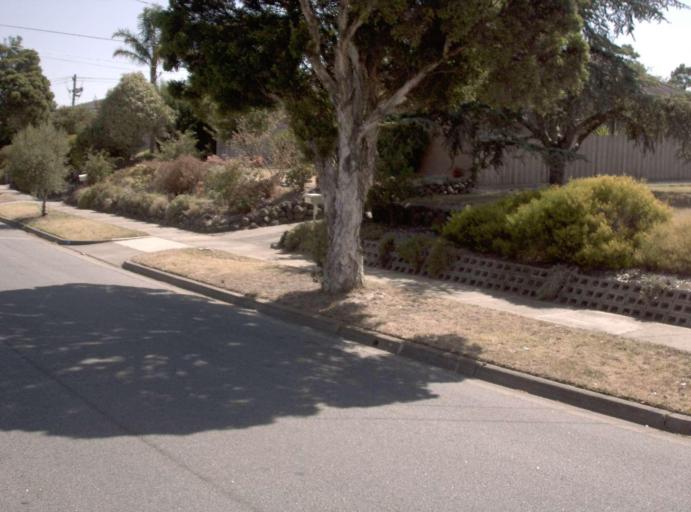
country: AU
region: Victoria
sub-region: Greater Dandenong
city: Noble Park North
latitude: -37.9554
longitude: 145.1908
